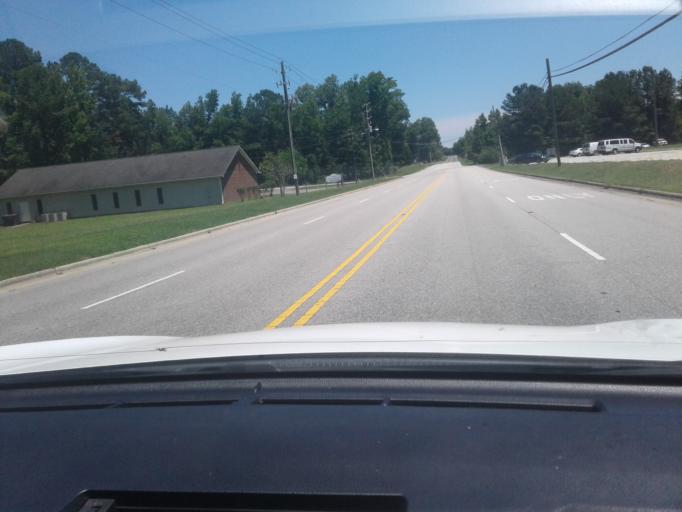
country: US
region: North Carolina
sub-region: Harnett County
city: Lillington
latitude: 35.3903
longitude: -78.8007
